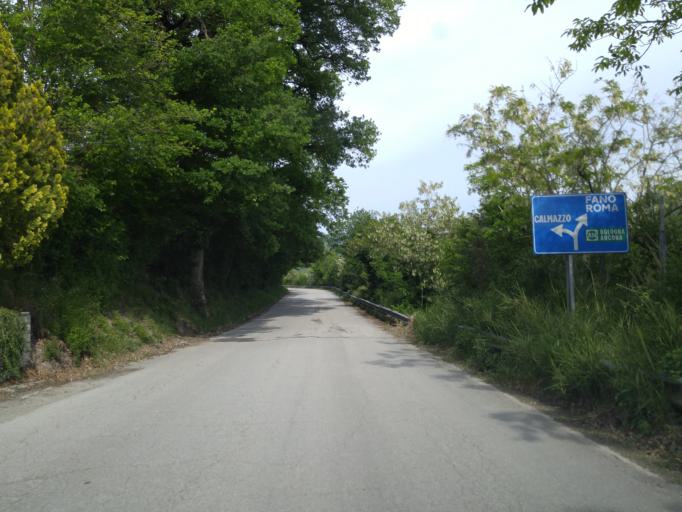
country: IT
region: The Marches
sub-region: Provincia di Pesaro e Urbino
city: Canavaccio
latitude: 43.6640
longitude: 12.7479
